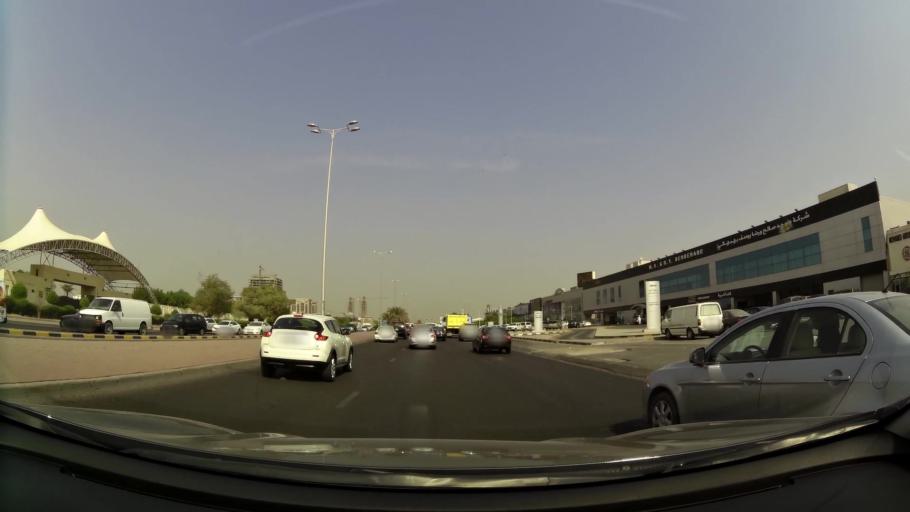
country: KW
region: Al Asimah
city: Ar Rabiyah
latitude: 29.3053
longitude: 47.9272
